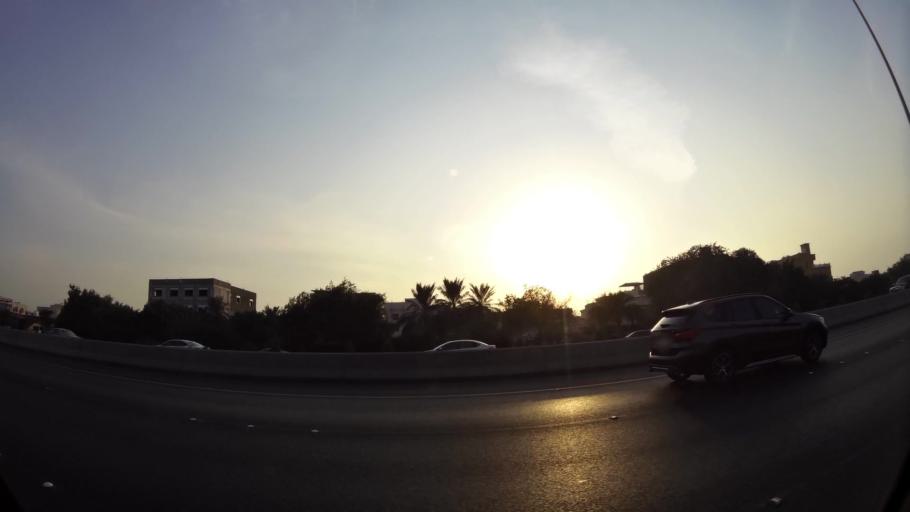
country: KW
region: Muhafazat Hawalli
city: Salwa
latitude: 29.3000
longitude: 48.0643
